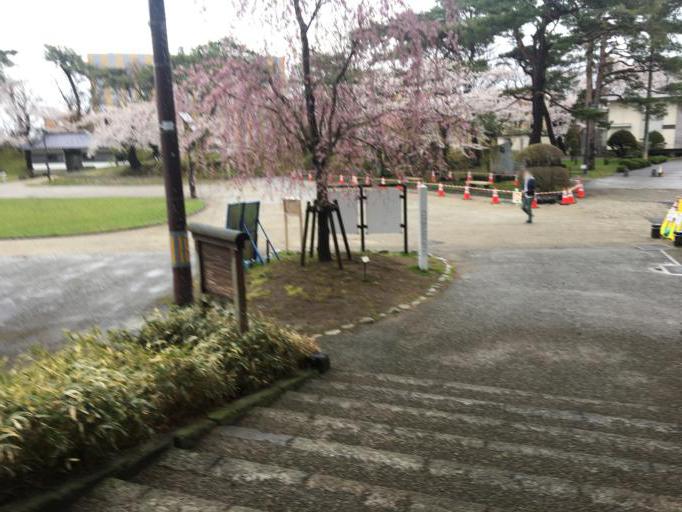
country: JP
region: Akita
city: Akita
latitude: 39.7206
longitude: 140.1244
